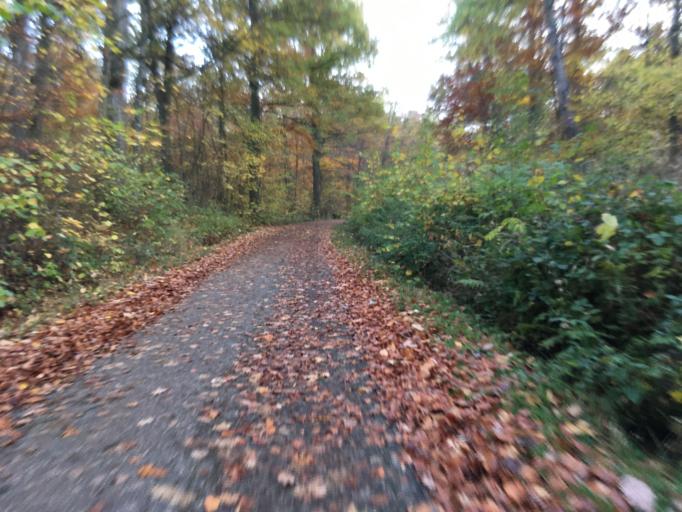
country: DE
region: Baden-Wuerttemberg
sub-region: Regierungsbezirk Stuttgart
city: Weinsberg
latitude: 49.1384
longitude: 9.2706
